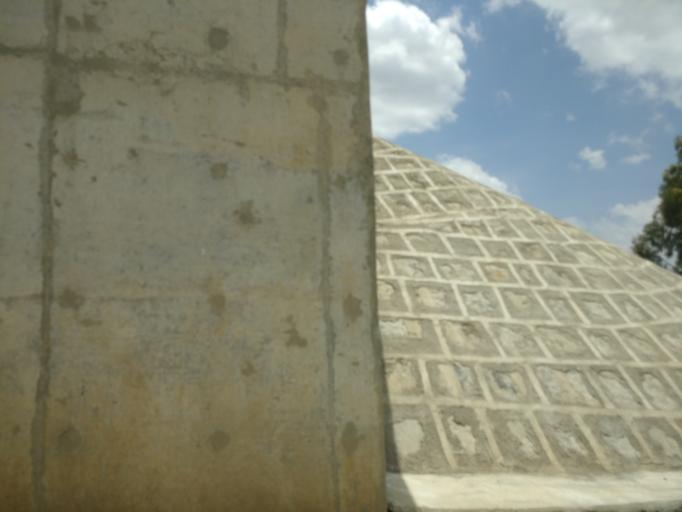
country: ET
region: Oromiya
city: Bishoftu
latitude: 8.7944
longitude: 38.9920
